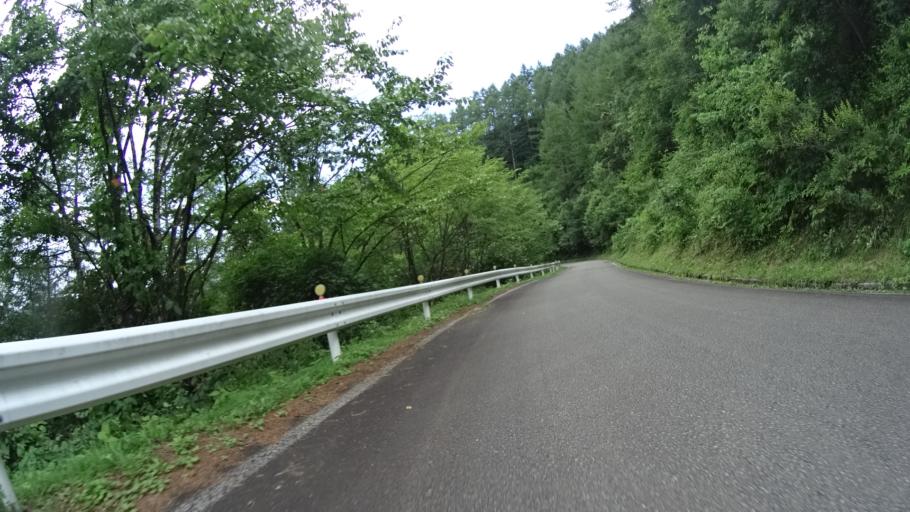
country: JP
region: Nagano
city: Saku
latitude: 36.0650
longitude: 138.6417
